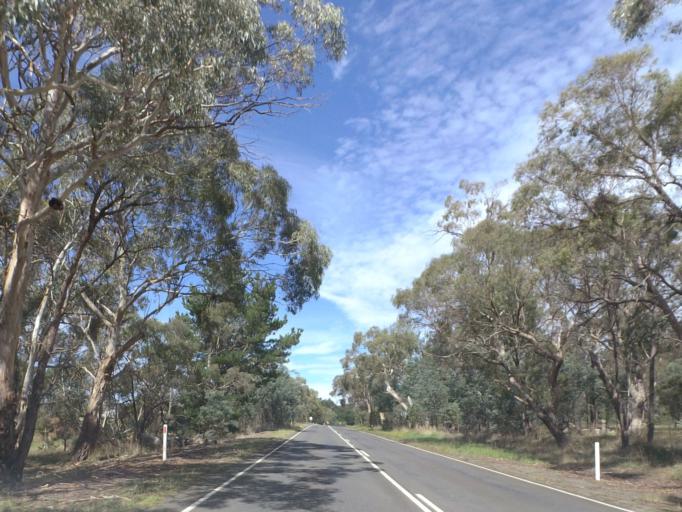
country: AU
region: Victoria
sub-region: Hume
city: Sunbury
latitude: -37.2980
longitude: 144.5119
